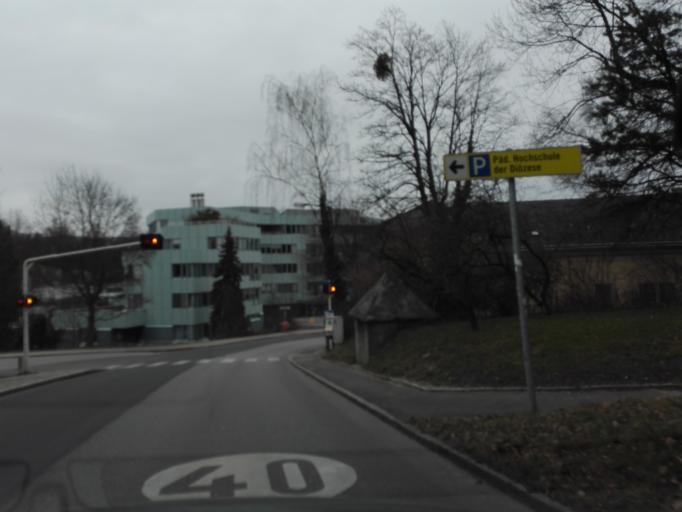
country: AT
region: Upper Austria
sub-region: Linz Stadt
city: Linz
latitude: 48.2974
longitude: 14.2752
